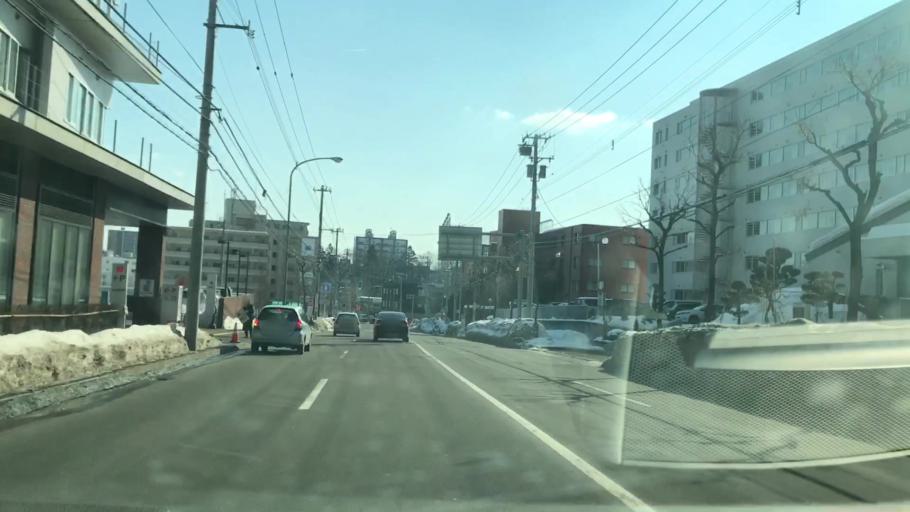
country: JP
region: Hokkaido
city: Sapporo
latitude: 43.0246
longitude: 141.3819
